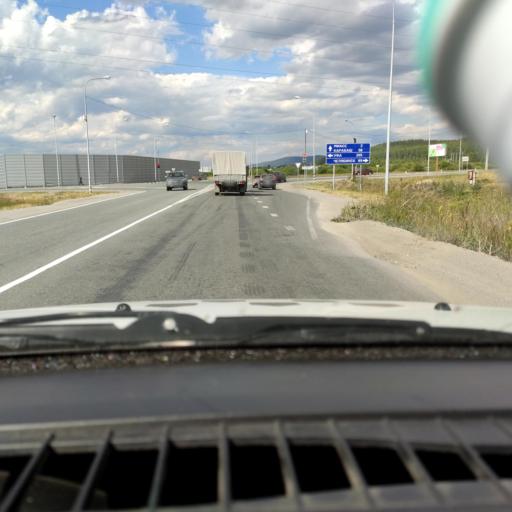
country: RU
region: Chelyabinsk
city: Miass
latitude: 54.9434
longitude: 60.0505
